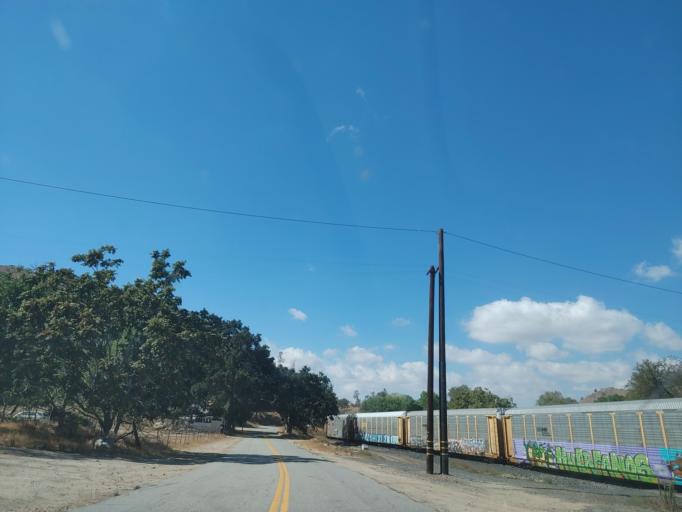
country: US
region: California
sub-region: Kern County
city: Bear Valley Springs
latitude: 35.2169
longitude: -118.5557
